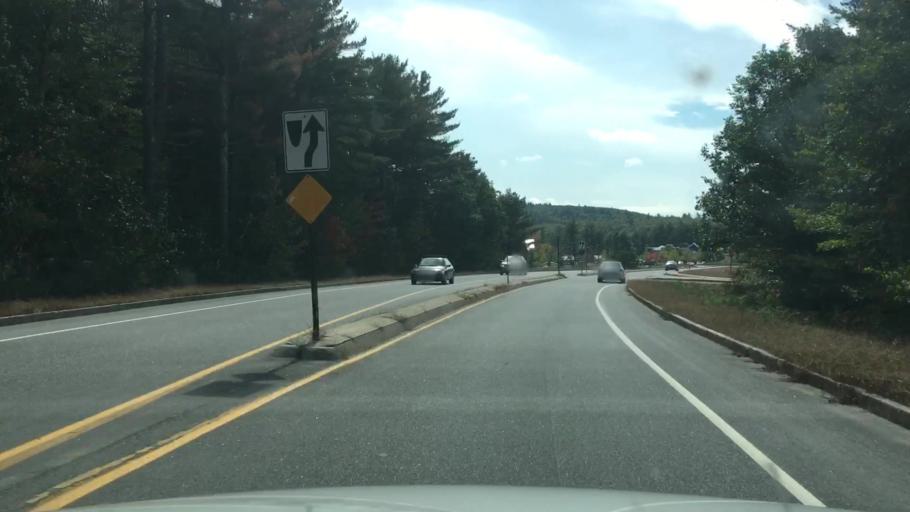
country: US
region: New Hampshire
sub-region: Carroll County
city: North Conway
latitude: 44.0230
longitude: -71.1090
